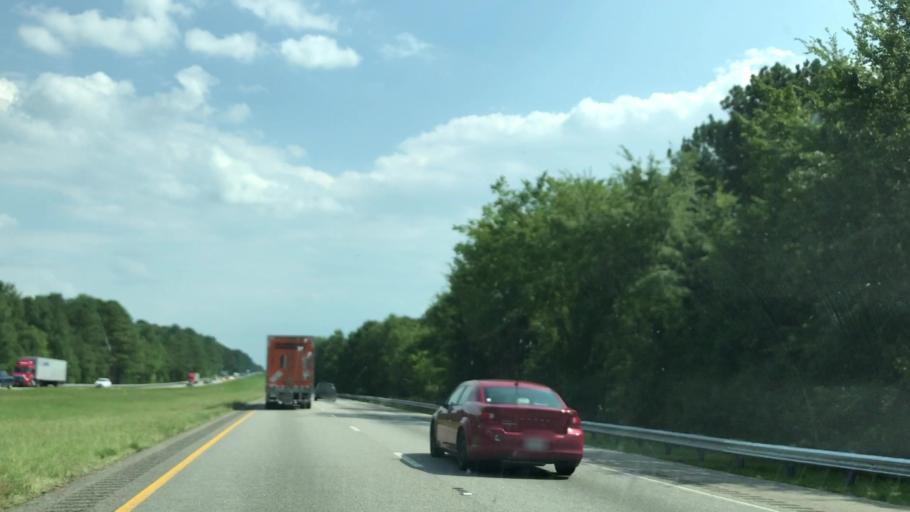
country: US
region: South Carolina
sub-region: Chester County
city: Eureka Mill
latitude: 34.6923
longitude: -81.0298
